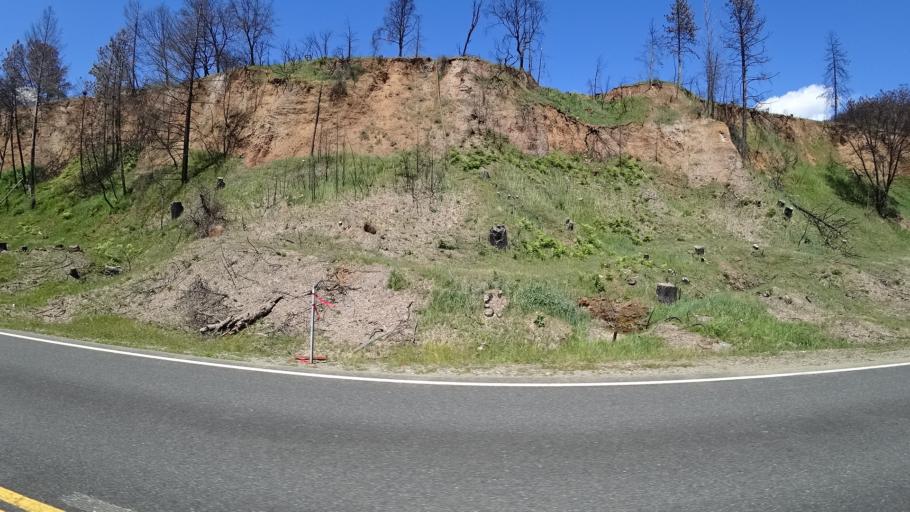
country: US
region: California
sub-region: Trinity County
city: Weaverville
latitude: 40.7653
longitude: -123.0804
